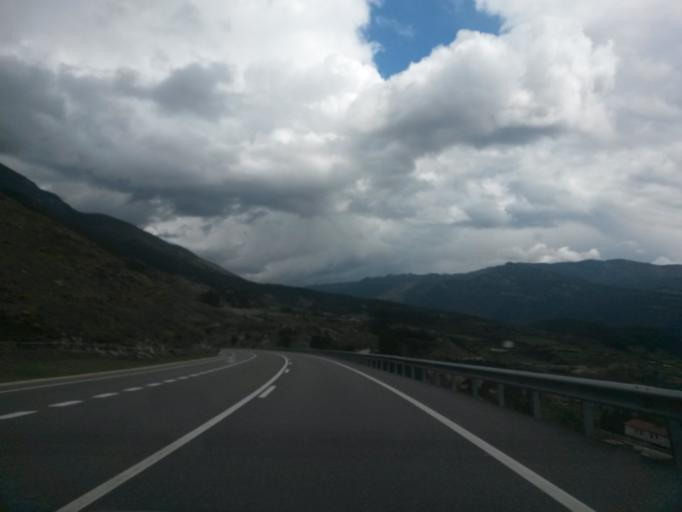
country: ES
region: Catalonia
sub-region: Provincia de Barcelona
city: Baga
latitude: 42.2585
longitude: 1.8584
